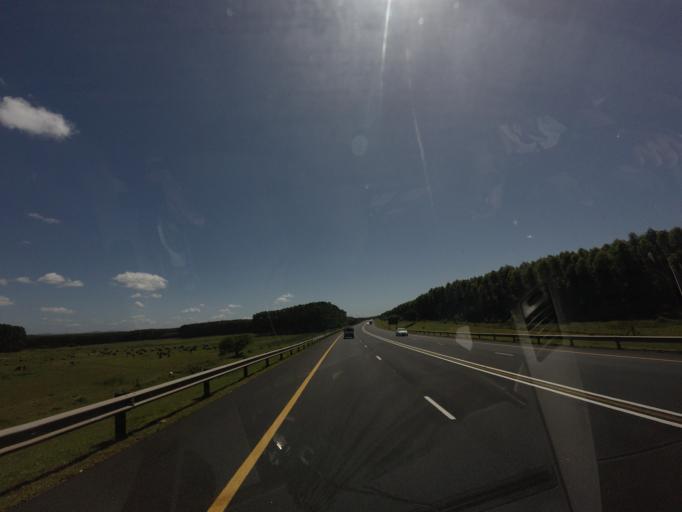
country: ZA
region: KwaZulu-Natal
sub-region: uThungulu District Municipality
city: Eshowe
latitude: -29.0288
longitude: 31.6609
